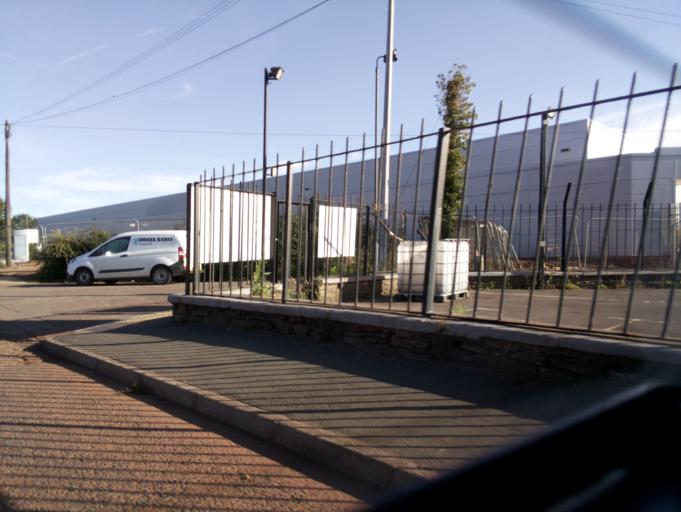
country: GB
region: England
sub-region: South Gloucestershire
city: Kingswood
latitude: 51.4420
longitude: -2.5000
